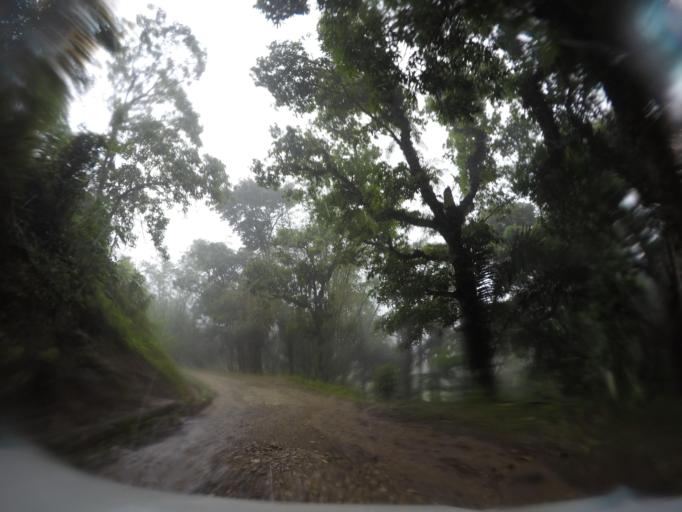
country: TL
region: Baucau
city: Venilale
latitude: -8.6425
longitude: 126.4031
